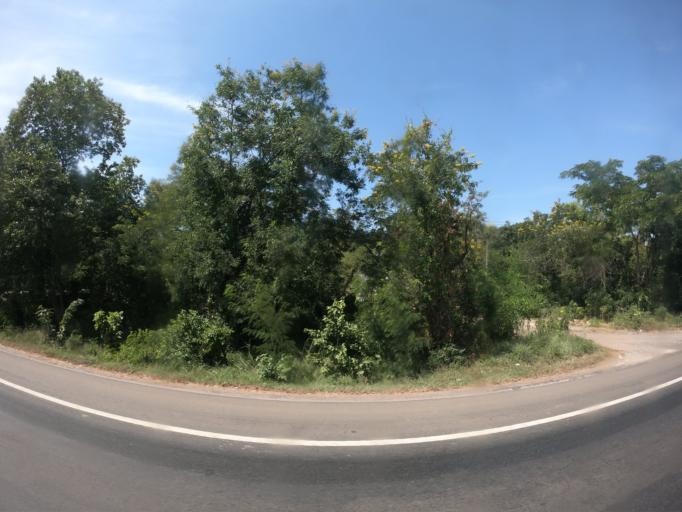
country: TH
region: Nakhon Ratchasima
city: Sida
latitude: 15.5547
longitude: 102.5497
